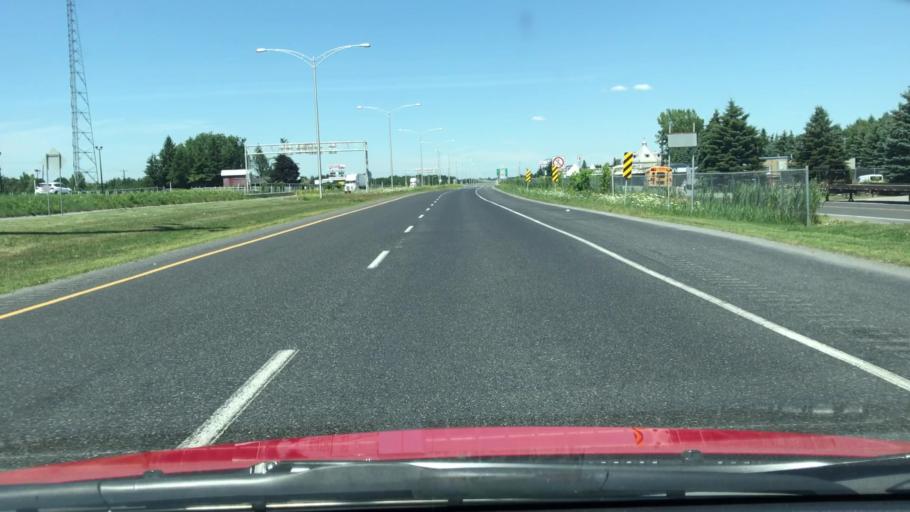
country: US
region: New York
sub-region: Clinton County
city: Champlain
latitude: 45.0131
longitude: -73.4524
